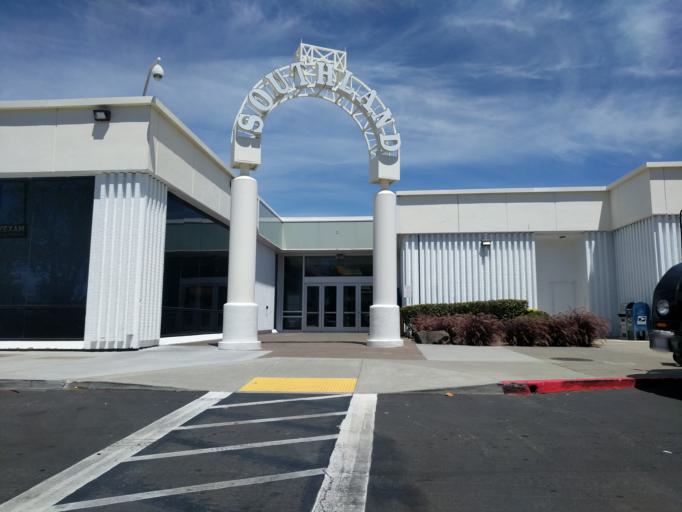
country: US
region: California
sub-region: Alameda County
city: Hayward
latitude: 37.6502
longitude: -122.1025
